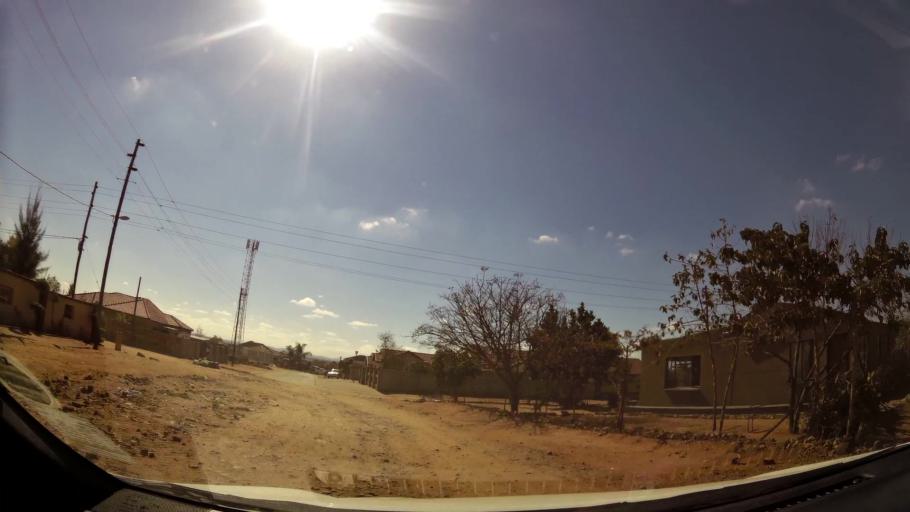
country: ZA
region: Limpopo
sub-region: Capricorn District Municipality
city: Polokwane
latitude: -23.8762
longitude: 29.4105
